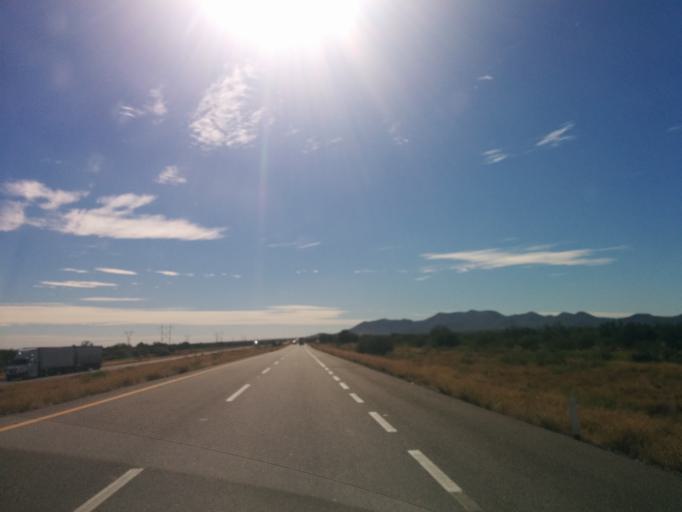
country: MX
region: Sonora
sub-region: San Miguel de Horcasitas
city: Las Mercedes [Agropecuaria]
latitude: 29.5756
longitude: -111.0186
